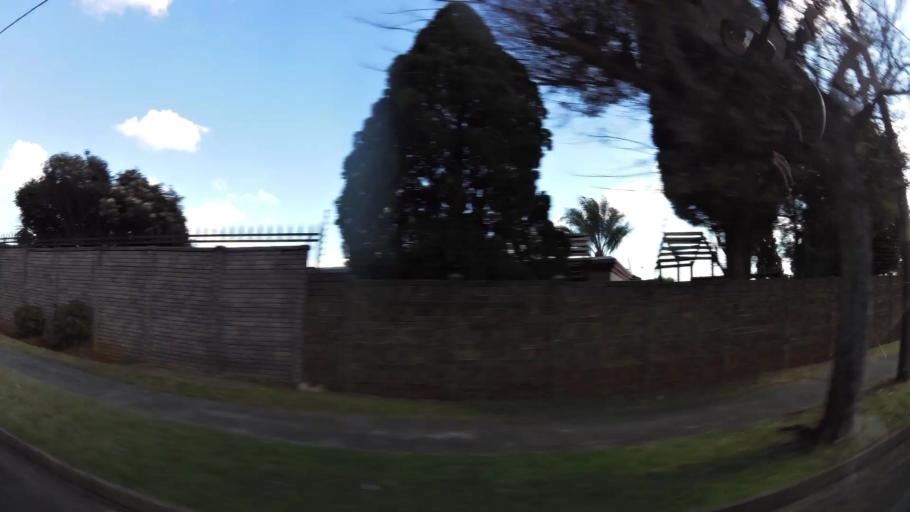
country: ZA
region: Gauteng
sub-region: City of Johannesburg Metropolitan Municipality
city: Roodepoort
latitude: -26.1359
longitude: 27.8301
